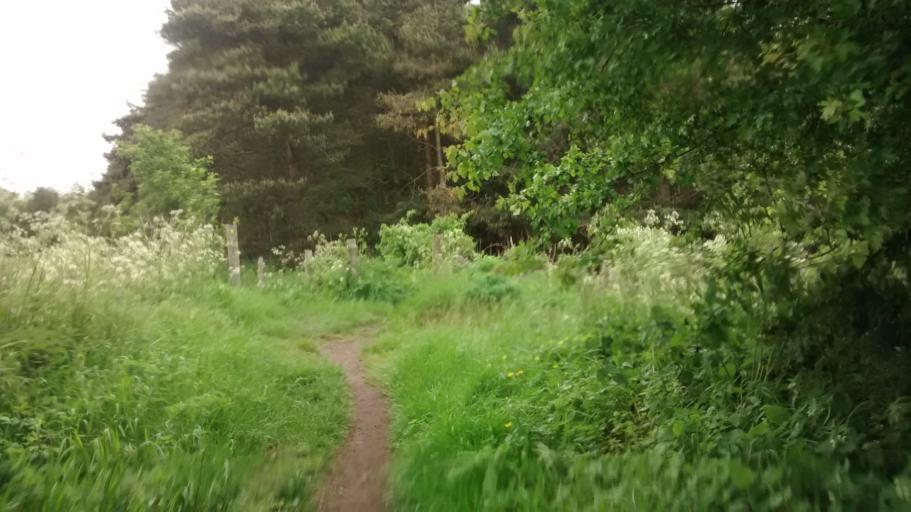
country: GB
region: England
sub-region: County Durham
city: Pittington
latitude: 54.7921
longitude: -1.4824
